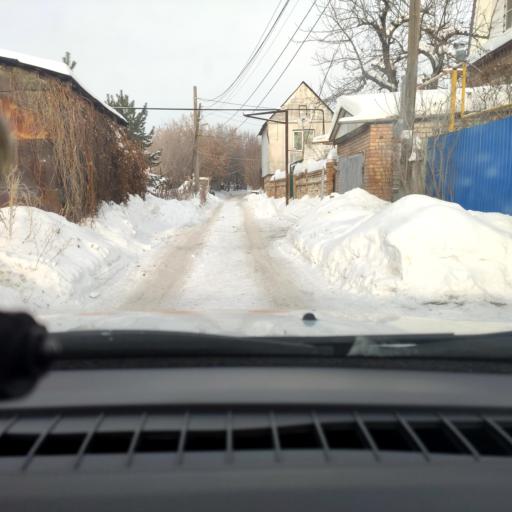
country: RU
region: Samara
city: Rozhdestveno
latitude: 53.1643
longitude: 50.0723
